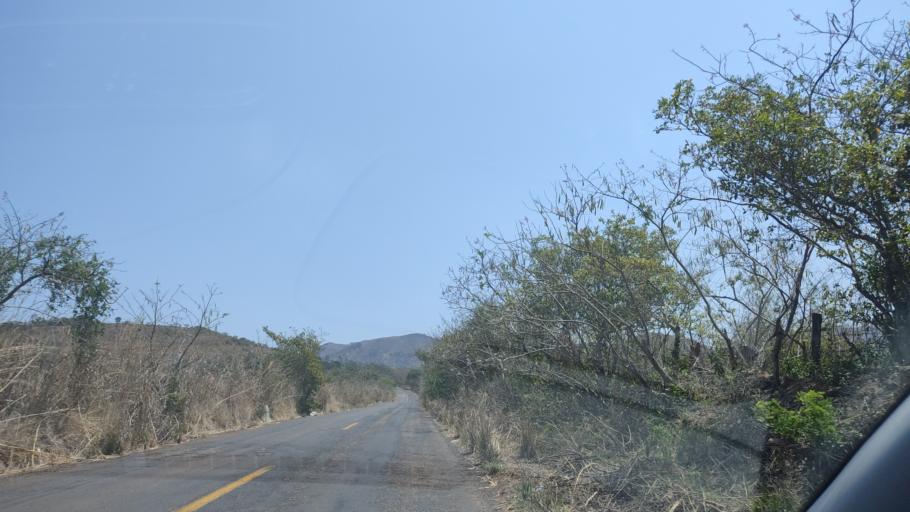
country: MX
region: Nayarit
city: Puga
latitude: 21.5786
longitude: -104.7687
